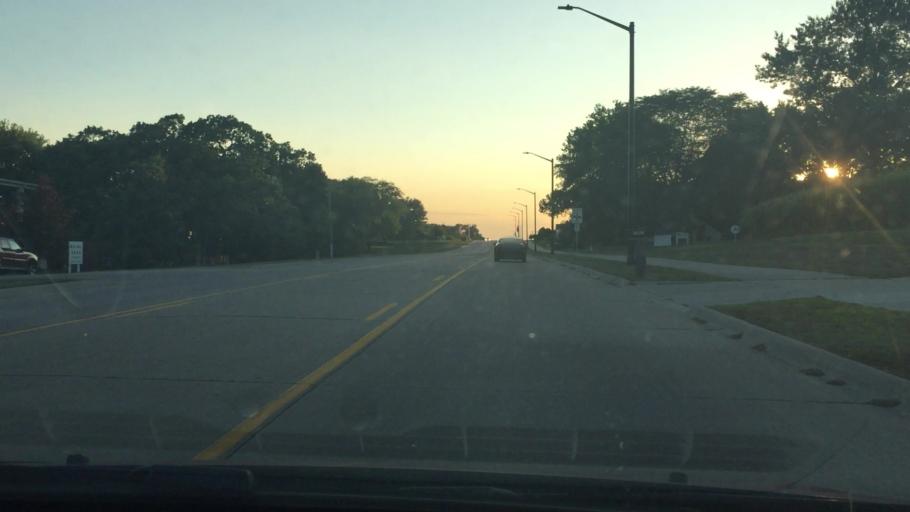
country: US
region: Iowa
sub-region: Muscatine County
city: Muscatine
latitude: 41.4359
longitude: -91.0678
